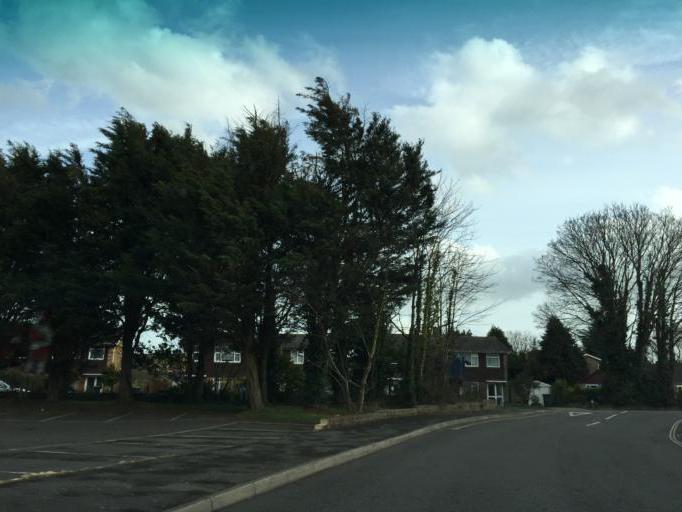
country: GB
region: England
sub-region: Hampshire
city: Gosport
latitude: 50.8150
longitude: -1.1530
